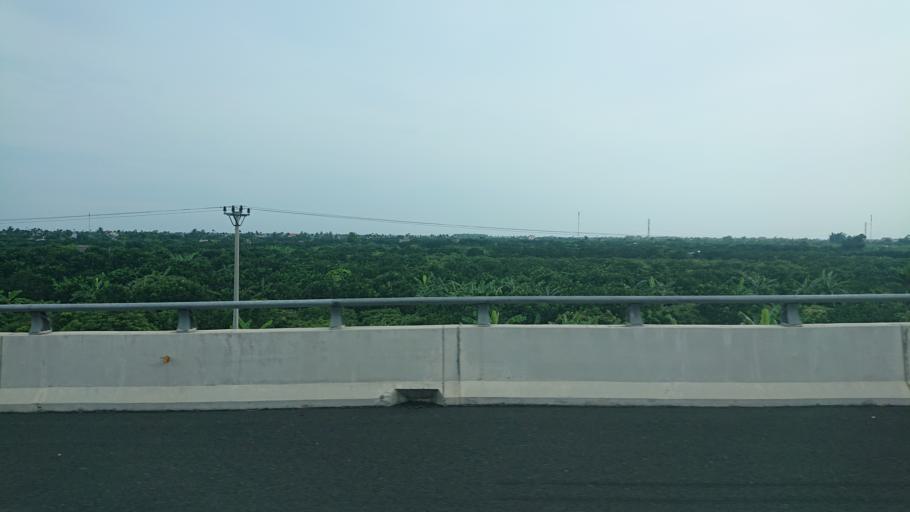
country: VN
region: Hai Duong
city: Tu Ky
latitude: 20.8318
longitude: 106.4454
